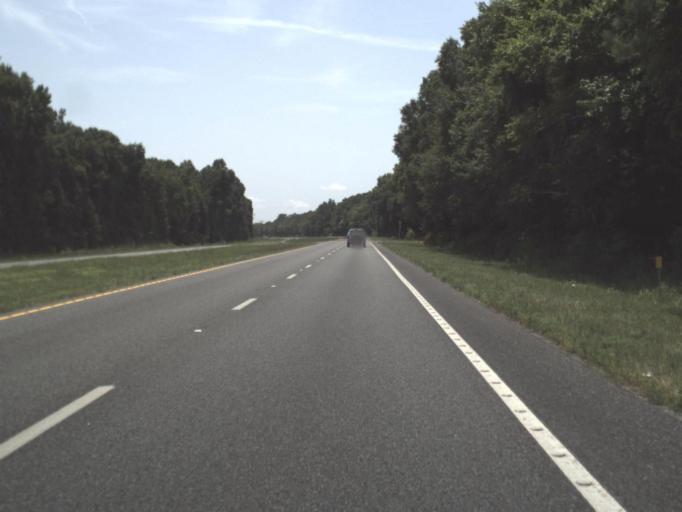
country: US
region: Florida
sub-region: Taylor County
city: Perry
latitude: 29.9343
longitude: -83.4460
